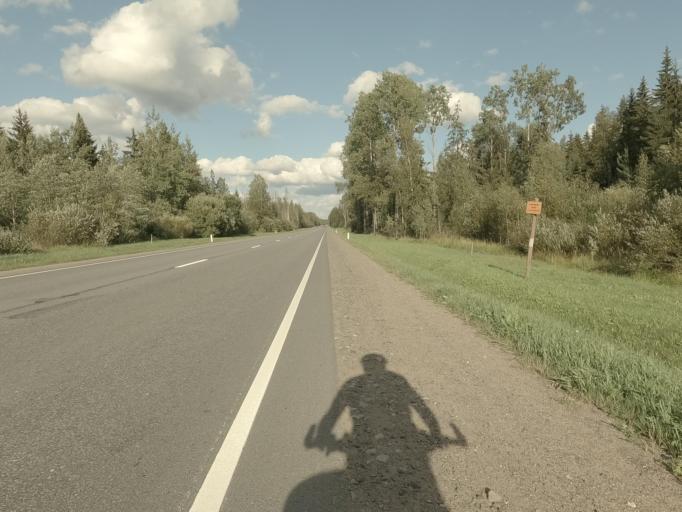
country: RU
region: Leningrad
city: Nikol'skoye
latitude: 59.6740
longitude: 30.9183
